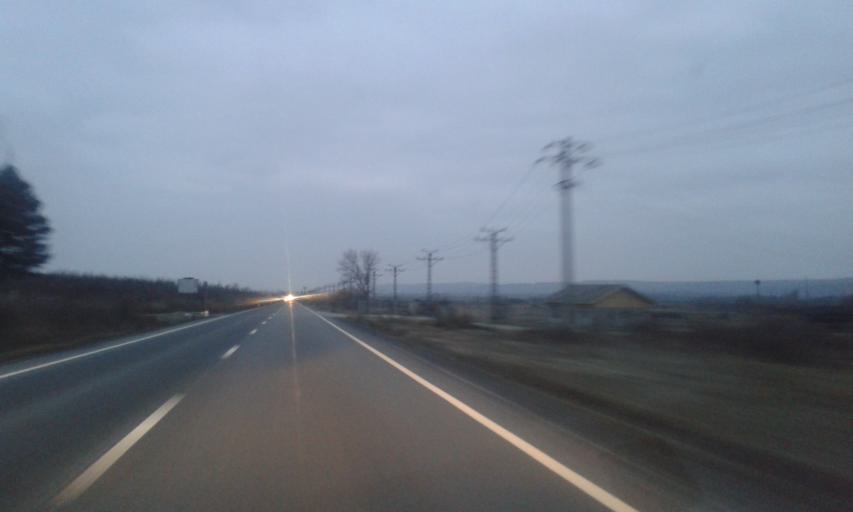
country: RO
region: Gorj
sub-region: Comuna Turcinesti
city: Turcinesti
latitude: 45.1286
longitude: 23.3619
